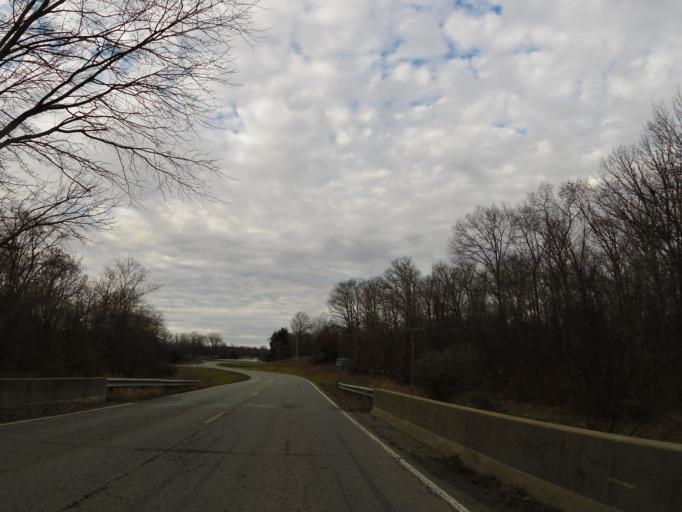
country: US
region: Illinois
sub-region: Jefferson County
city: Mount Vernon
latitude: 38.3787
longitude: -89.0323
